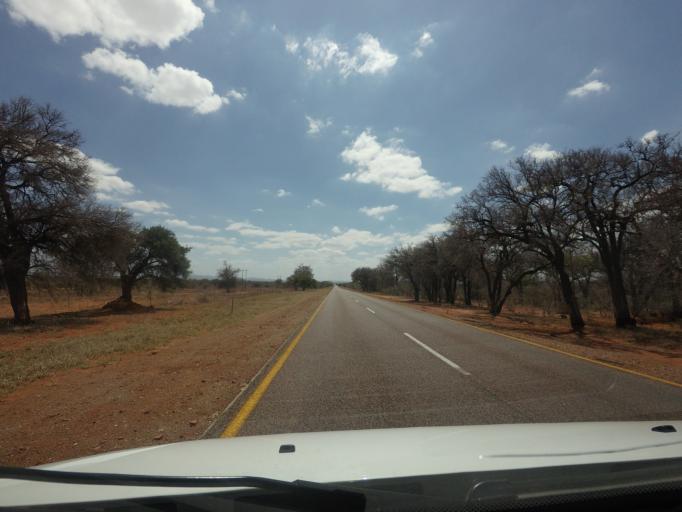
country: ZA
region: Limpopo
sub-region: Capricorn District Municipality
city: Dendron
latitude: -23.5525
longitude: 28.7390
